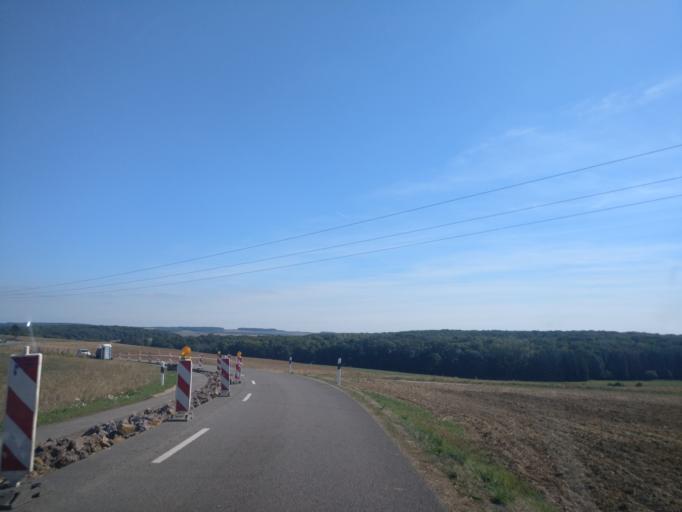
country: LU
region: Grevenmacher
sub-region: Canton de Grevenmacher
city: Flaxweiler
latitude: 49.6614
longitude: 6.3578
